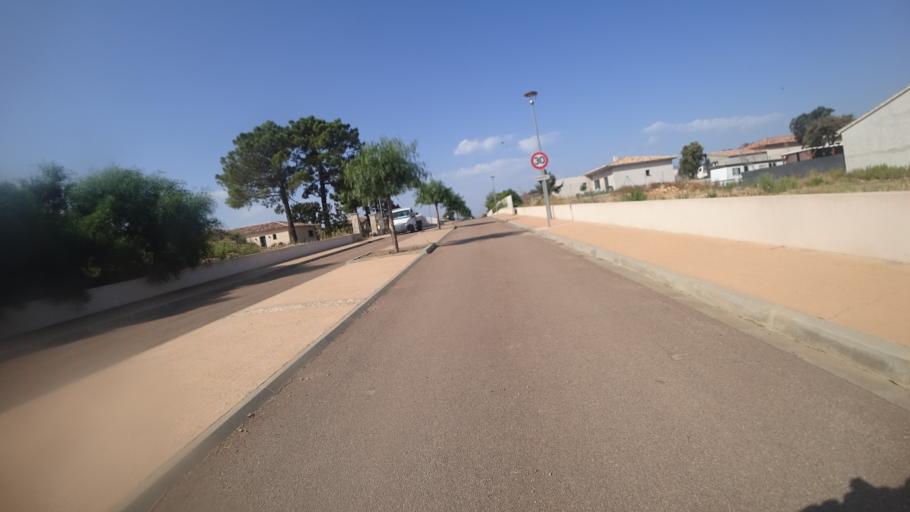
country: FR
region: Corsica
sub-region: Departement de la Corse-du-Sud
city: Porto-Vecchio
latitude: 41.6403
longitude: 9.3394
